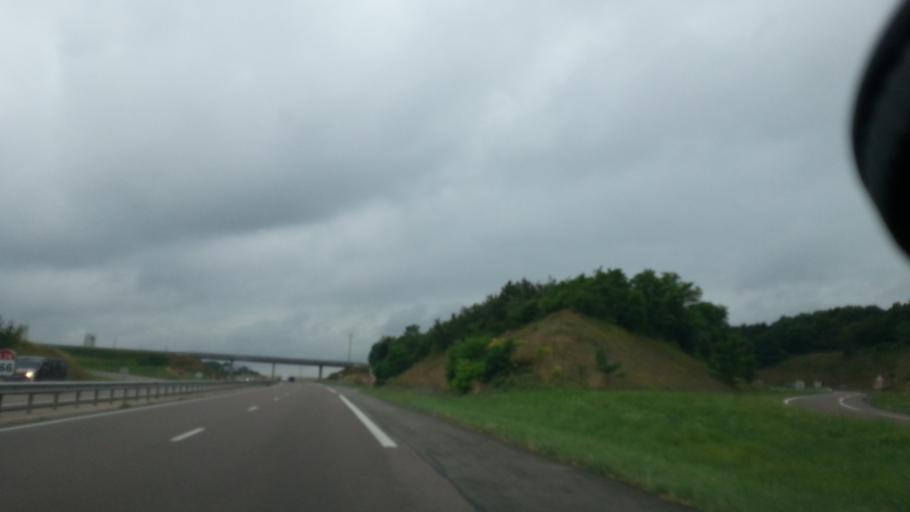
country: FR
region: Franche-Comte
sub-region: Departement du Jura
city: Dole
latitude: 47.1383
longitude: 5.5135
